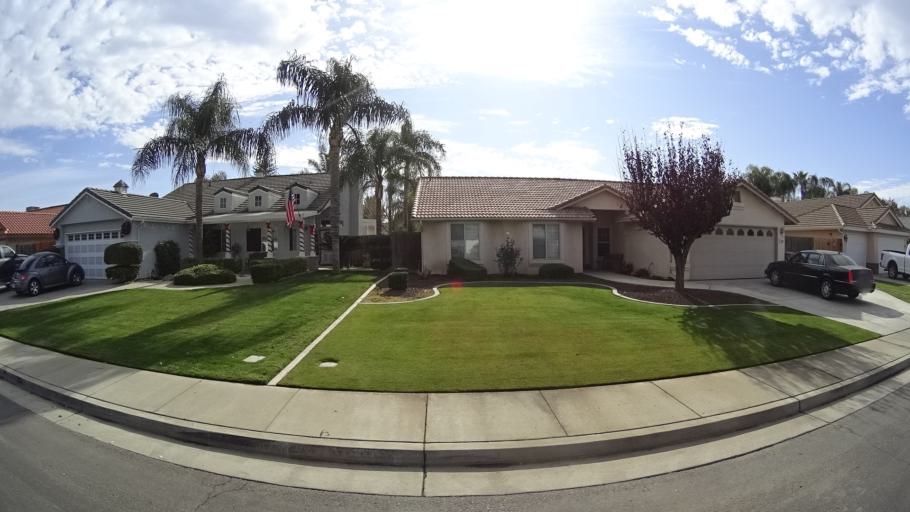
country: US
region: California
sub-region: Kern County
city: Greenacres
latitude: 35.4066
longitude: -119.1253
